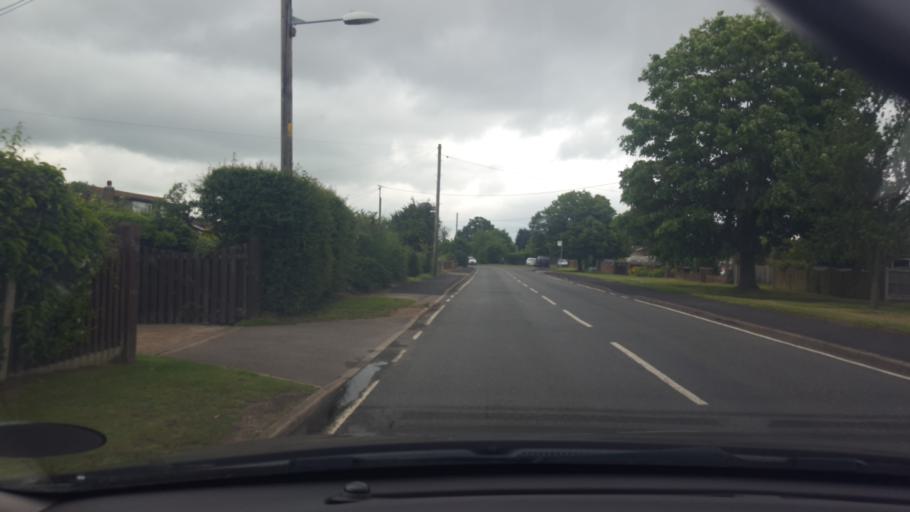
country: GB
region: England
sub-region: Essex
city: Brightlingsea
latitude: 51.7939
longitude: 1.0433
